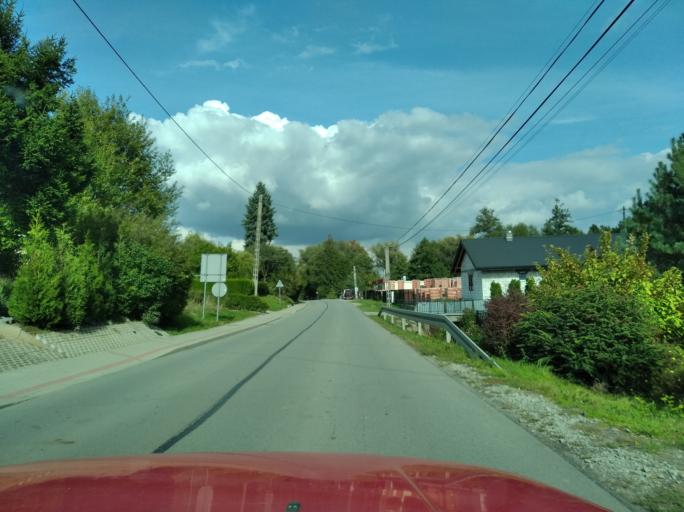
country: PL
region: Subcarpathian Voivodeship
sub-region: Powiat rzeszowski
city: Tyczyn
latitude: 49.9422
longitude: 22.0202
